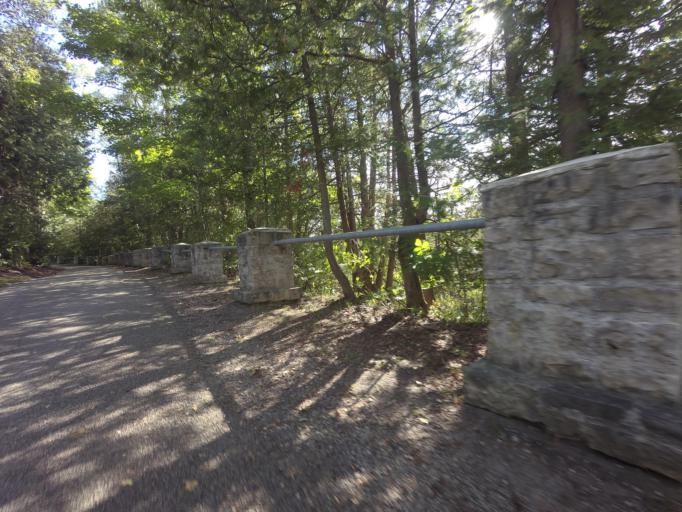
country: CA
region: Ontario
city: Waterloo
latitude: 43.6774
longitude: -80.4452
